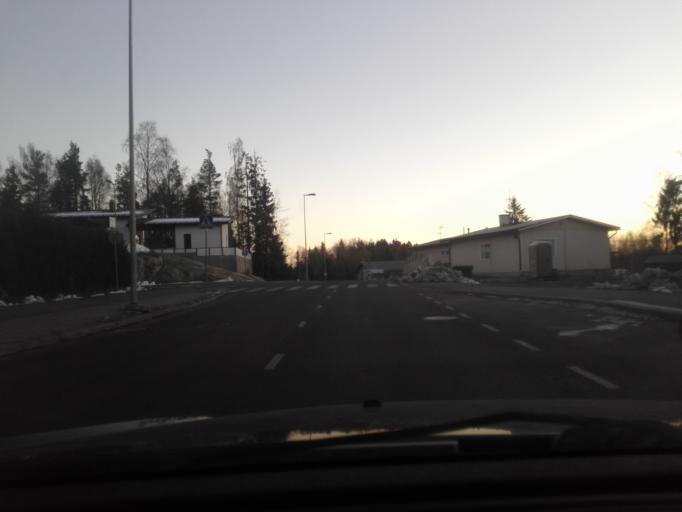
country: FI
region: Uusimaa
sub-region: Helsinki
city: Kerava
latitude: 60.3428
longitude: 25.1273
